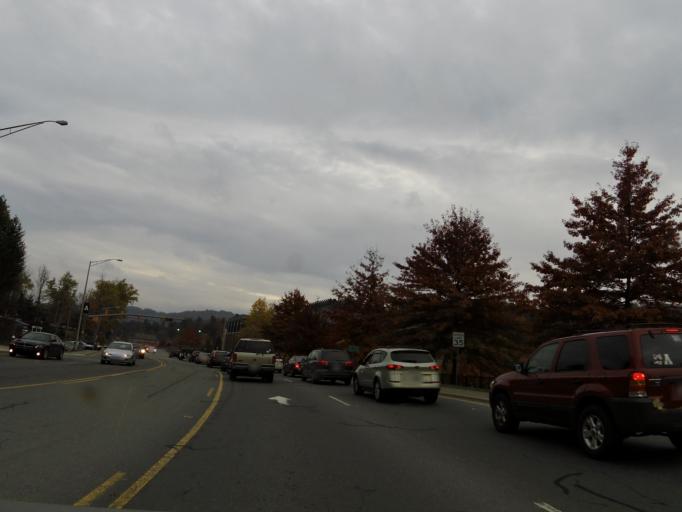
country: US
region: North Carolina
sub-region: Watauga County
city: Boone
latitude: 36.2125
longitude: -81.6759
